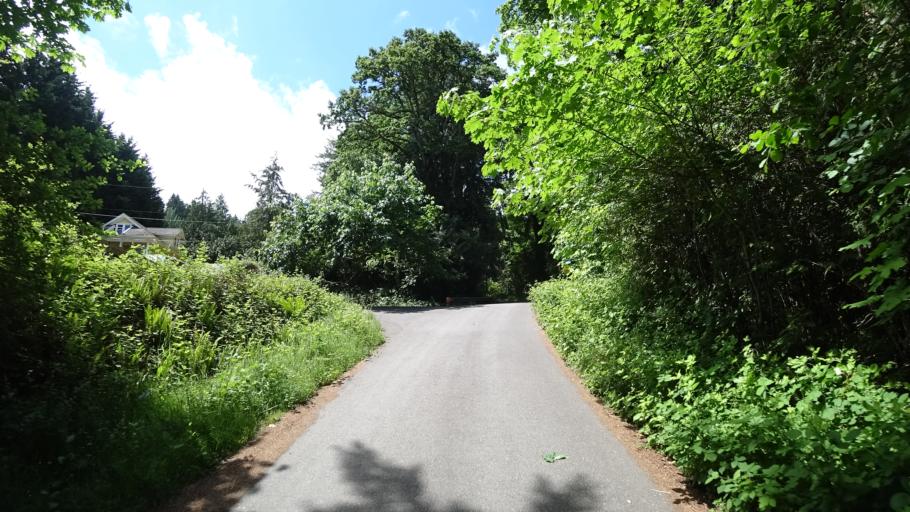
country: US
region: Oregon
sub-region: Washington County
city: West Haven
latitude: 45.5856
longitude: -122.7757
